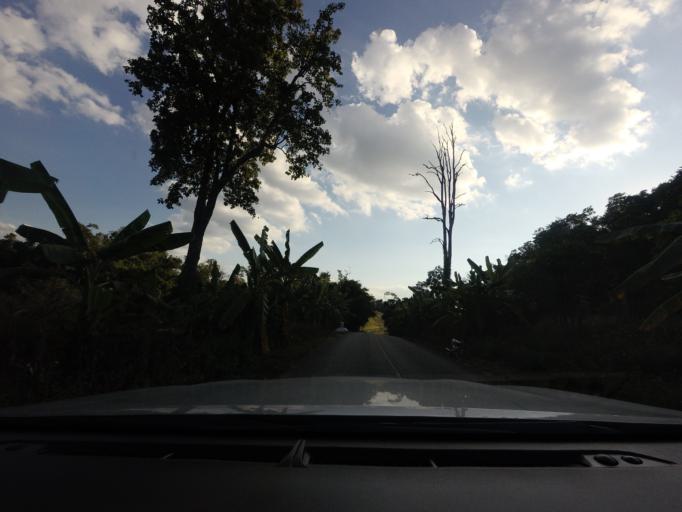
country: TH
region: Chiang Mai
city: Phrao
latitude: 19.5323
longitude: 99.1601
